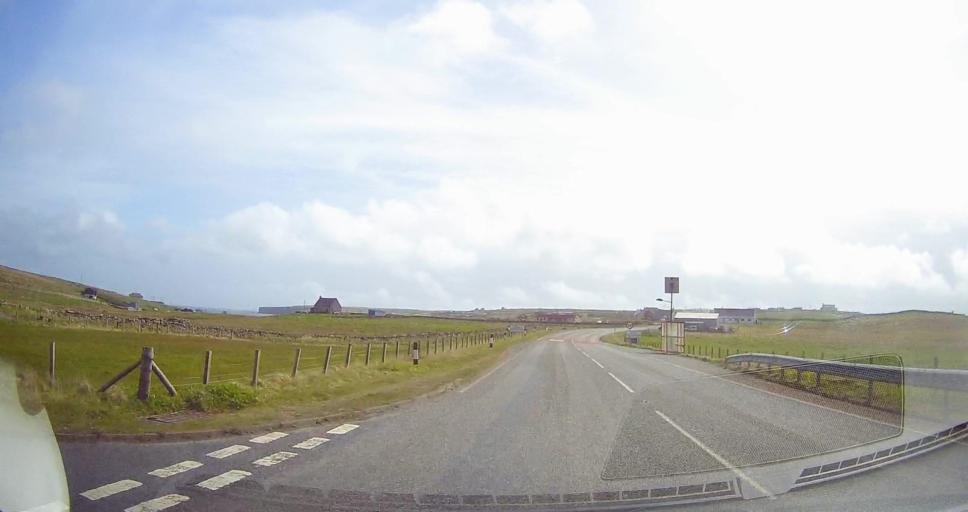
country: GB
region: Scotland
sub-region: Shetland Islands
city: Sandwick
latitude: 59.9281
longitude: -1.2974
